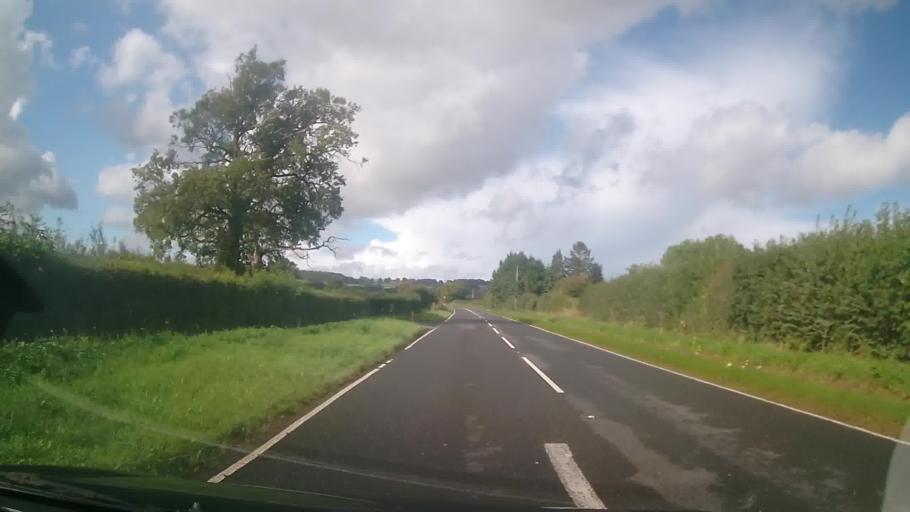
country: GB
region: England
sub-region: Gloucestershire
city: Moreton in Marsh
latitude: 51.9887
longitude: -1.7197
